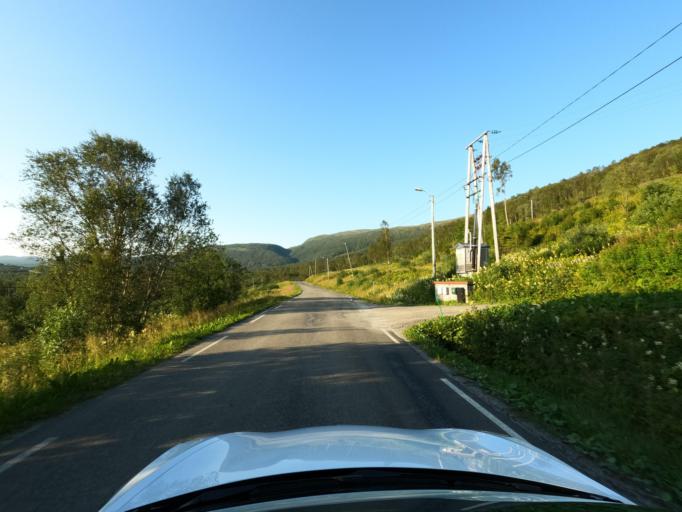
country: NO
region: Nordland
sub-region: Ballangen
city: Ballangen
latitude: 68.5199
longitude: 16.7585
